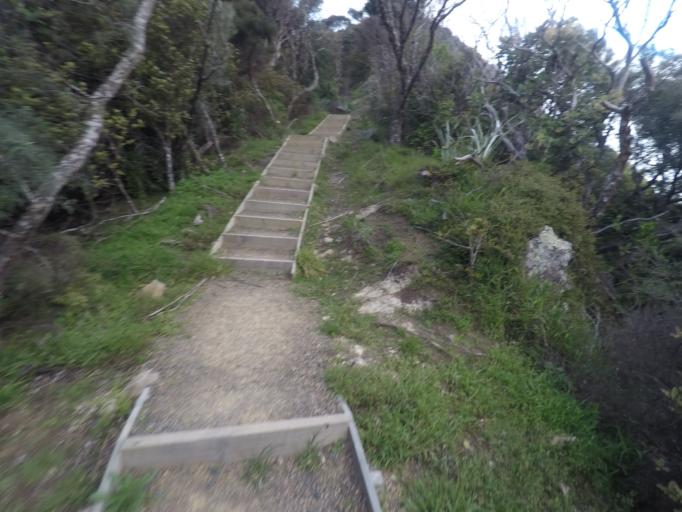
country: NZ
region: Auckland
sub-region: Auckland
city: Muriwai Beach
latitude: -36.9801
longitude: 174.4721
